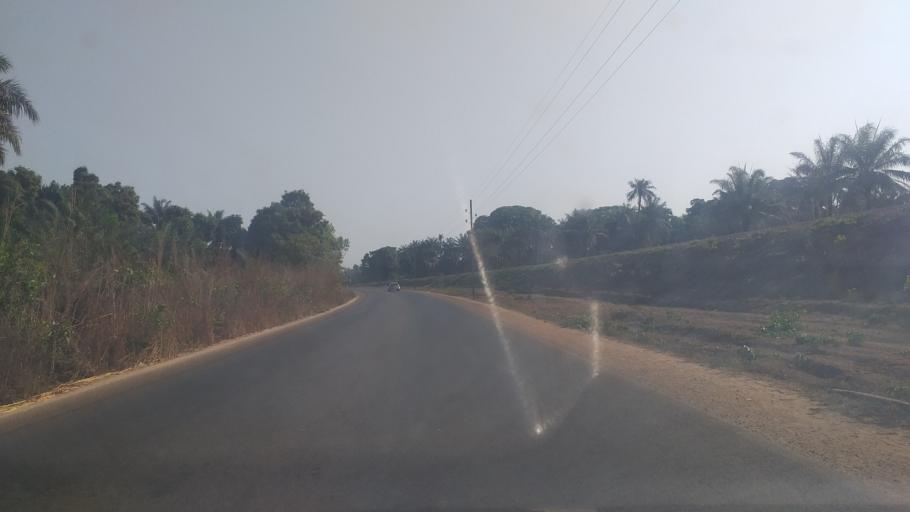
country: GN
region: Boke
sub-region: Boke Prefecture
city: Kamsar
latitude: 10.7123
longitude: -14.5233
